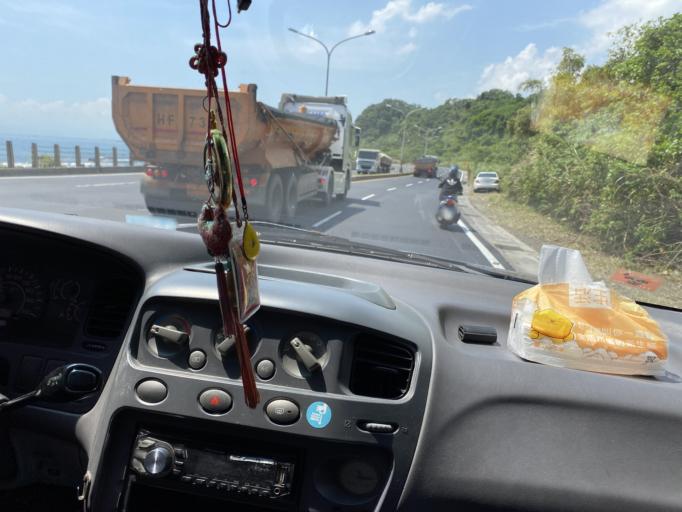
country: TW
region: Taiwan
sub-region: Yilan
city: Yilan
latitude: 24.8974
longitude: 121.8616
